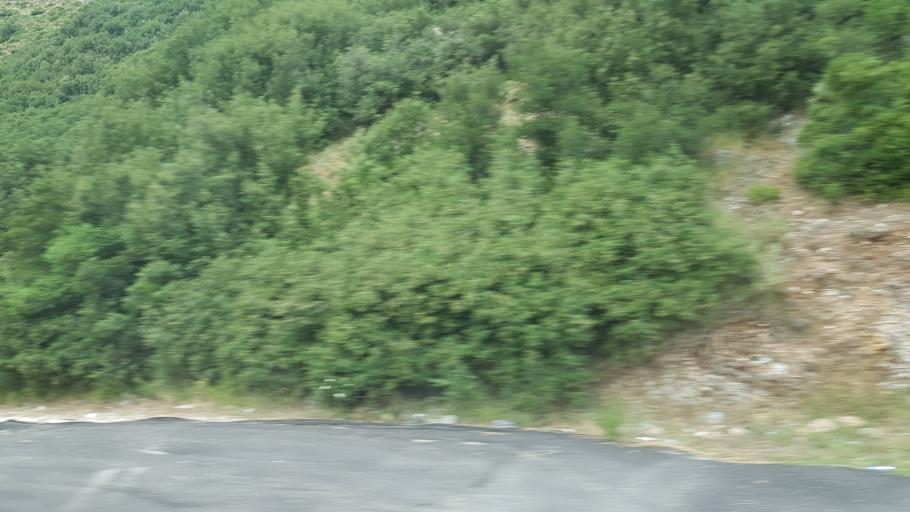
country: AL
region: Fier
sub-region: Rrethi i Mallakastres
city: Kute
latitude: 40.5110
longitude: 19.7521
